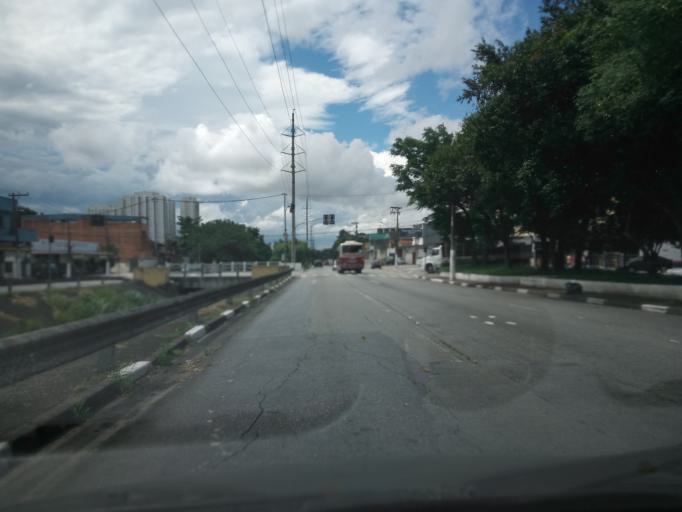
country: BR
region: Sao Paulo
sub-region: Sao Bernardo Do Campo
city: Sao Bernardo do Campo
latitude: -23.7022
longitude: -46.5767
